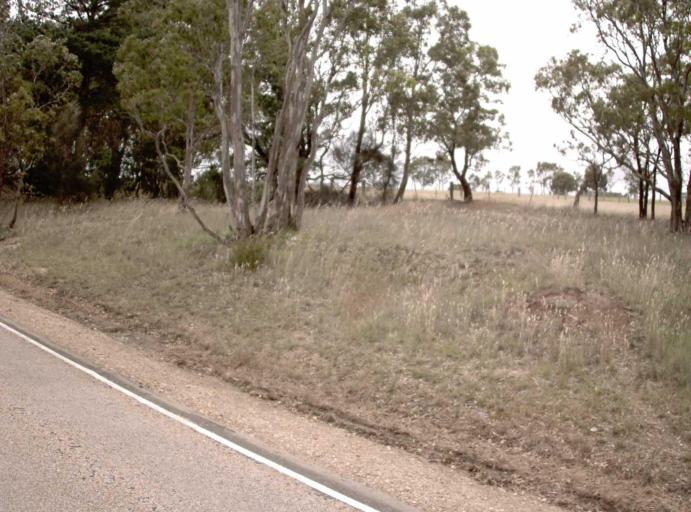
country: AU
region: Victoria
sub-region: Wellington
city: Sale
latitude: -37.9470
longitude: 147.0896
